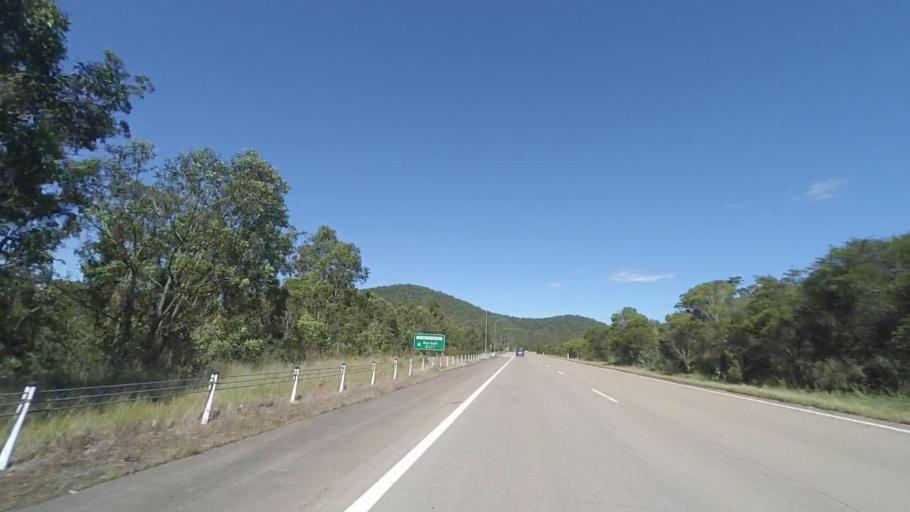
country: AU
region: New South Wales
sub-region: Port Stephens Shire
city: Port Stephens
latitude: -32.6330
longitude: 152.0017
